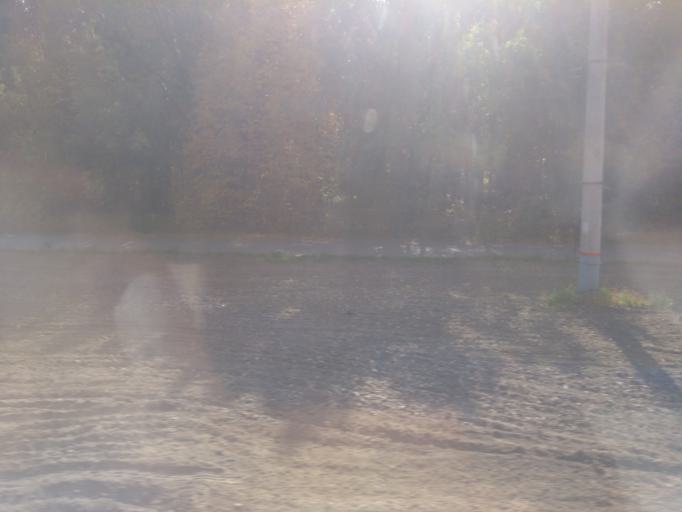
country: RU
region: Tatarstan
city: Aysha
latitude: 55.8417
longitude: 48.5807
